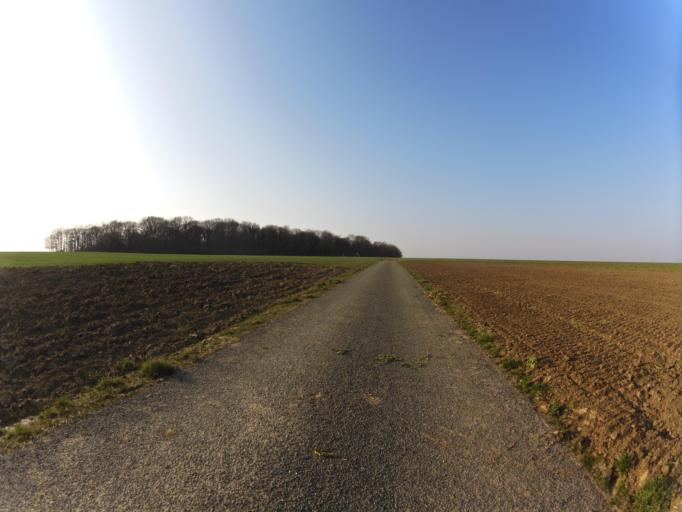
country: DE
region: Bavaria
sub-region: Regierungsbezirk Unterfranken
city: Geroldshausen
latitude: 49.6692
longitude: 9.9149
